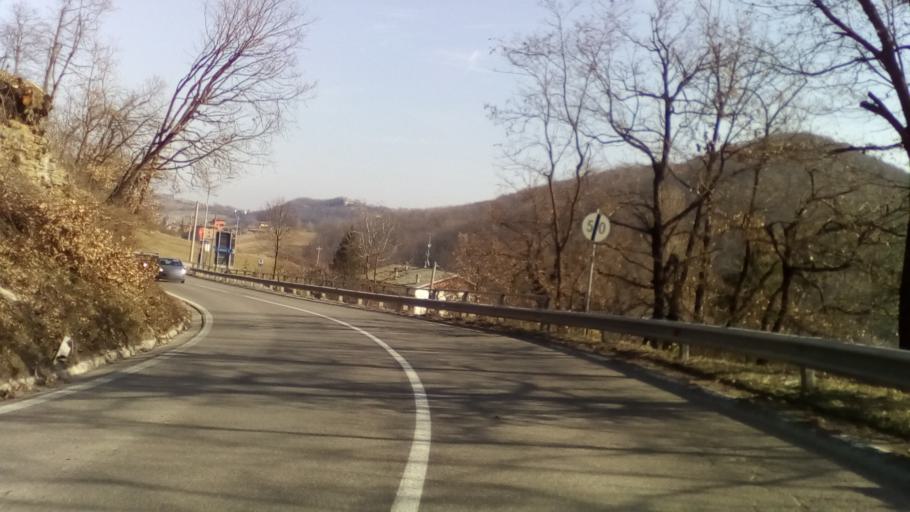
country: IT
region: Emilia-Romagna
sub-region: Provincia di Modena
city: Pavullo nel Frignano
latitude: 44.3075
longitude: 10.8178
